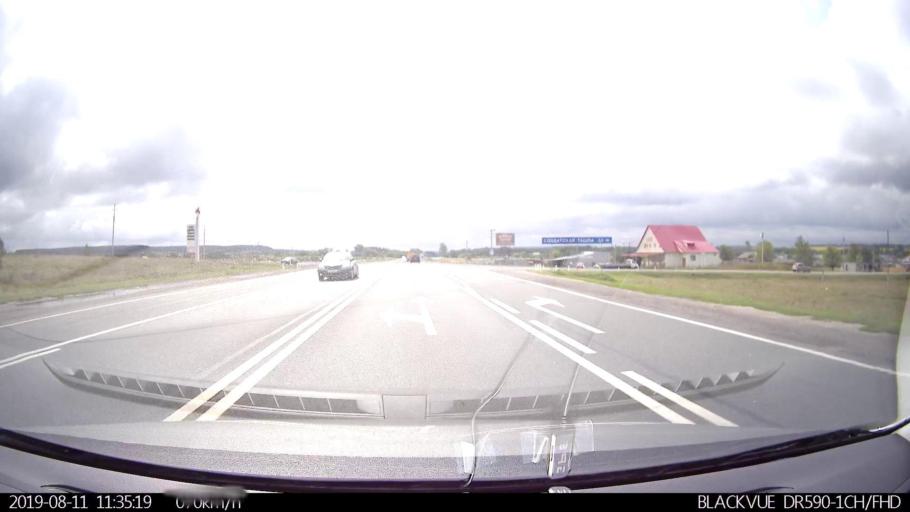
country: RU
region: Ulyanovsk
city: Silikatnyy
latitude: 54.0079
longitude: 48.2191
